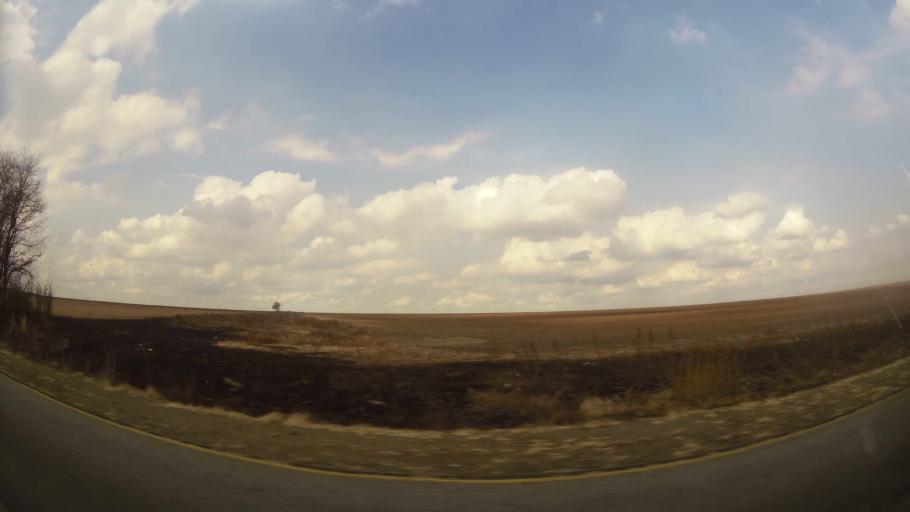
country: ZA
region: Orange Free State
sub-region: Fezile Dabi District Municipality
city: Sasolburg
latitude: -26.8333
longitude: 27.8973
